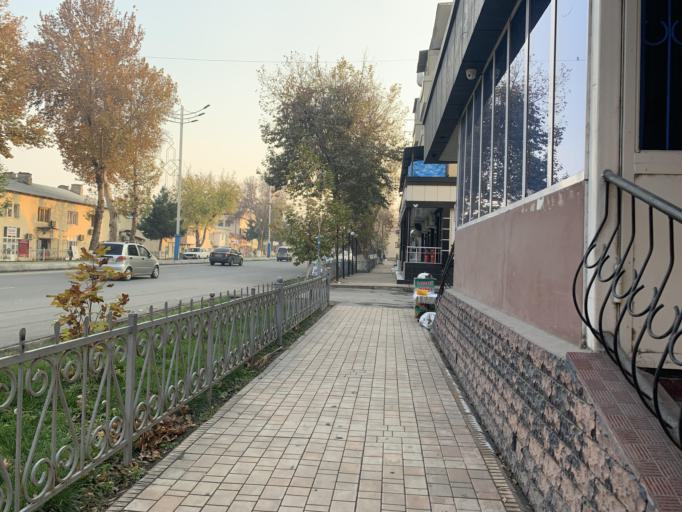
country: UZ
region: Fergana
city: Qo`qon
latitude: 40.5286
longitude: 70.9390
